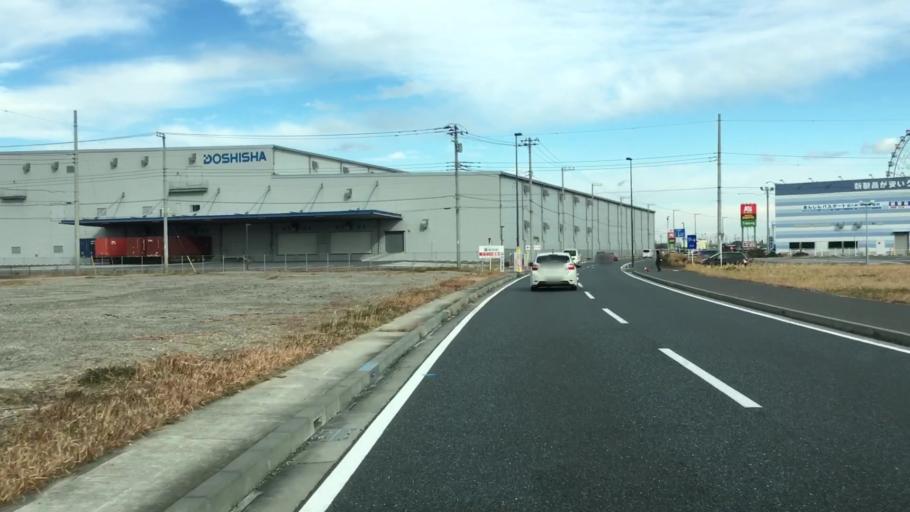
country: JP
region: Chiba
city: Kisarazu
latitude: 35.4382
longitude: 139.9278
